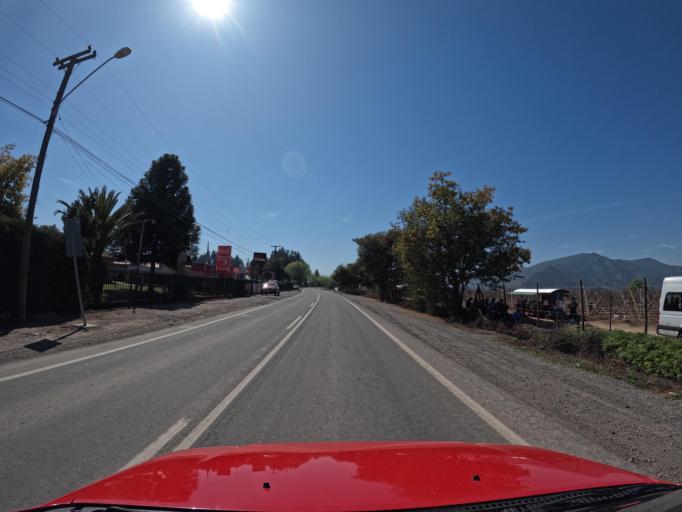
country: CL
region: Maule
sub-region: Provincia de Curico
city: Rauco
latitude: -35.0345
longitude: -71.4460
